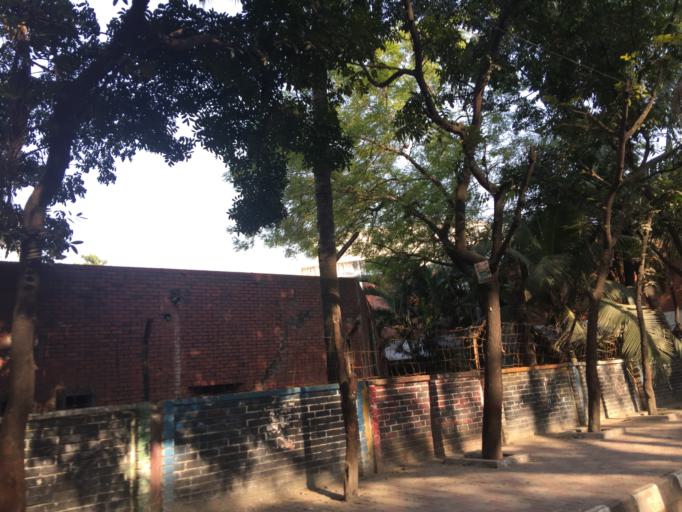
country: BD
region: Dhaka
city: Azimpur
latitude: 23.7266
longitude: 90.3908
